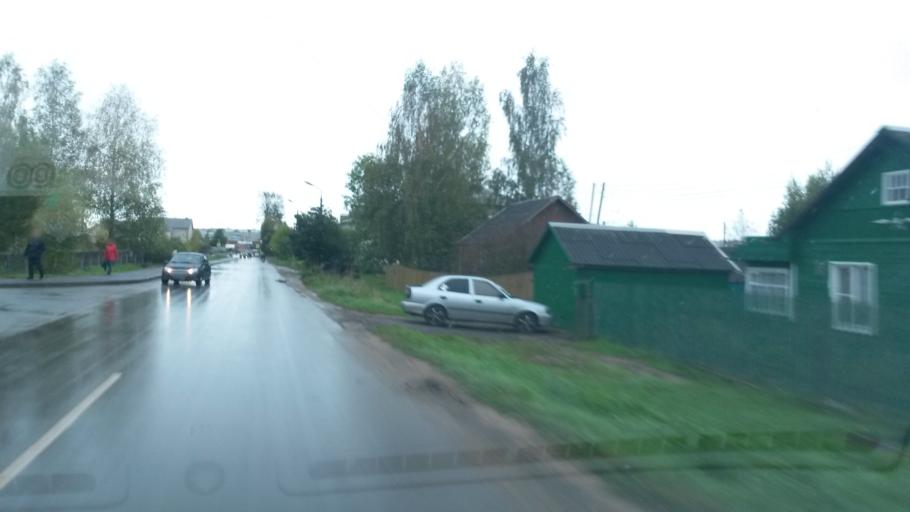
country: RU
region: Jaroslavl
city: Gavrilov-Yam
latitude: 57.3108
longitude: 39.8654
